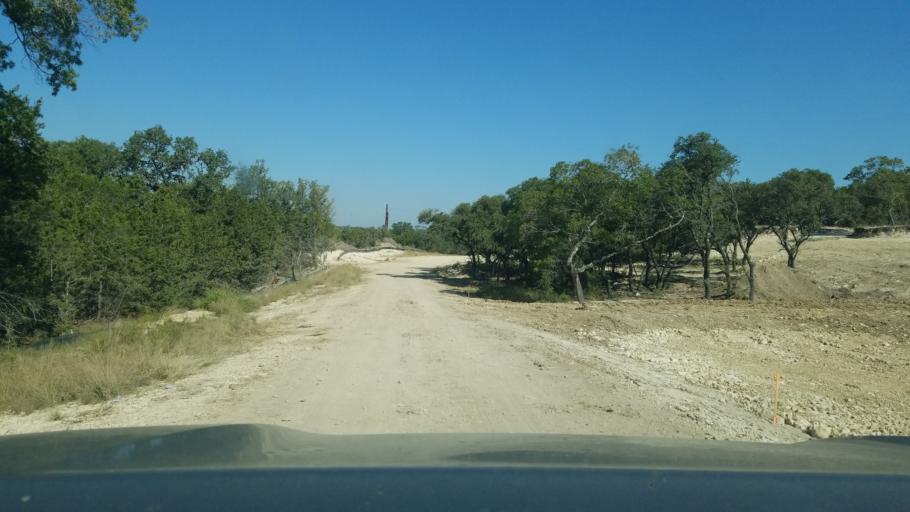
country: US
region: Texas
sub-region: Kendall County
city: Boerne
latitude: 29.7574
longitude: -98.7193
